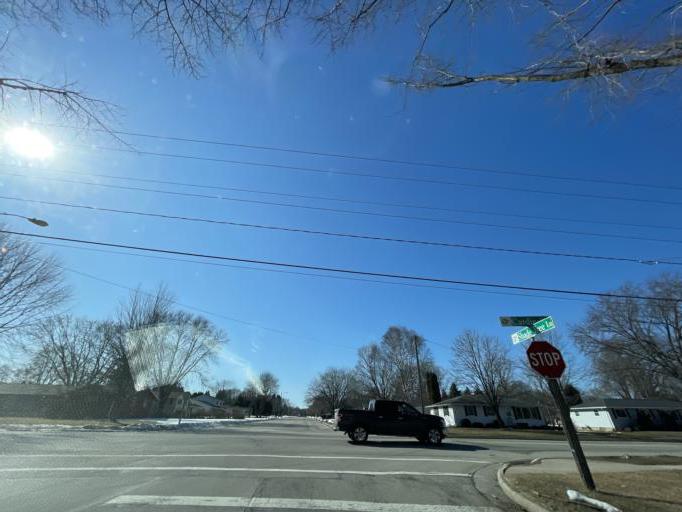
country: US
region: Wisconsin
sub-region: Brown County
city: Howard
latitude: 44.5685
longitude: -88.0845
